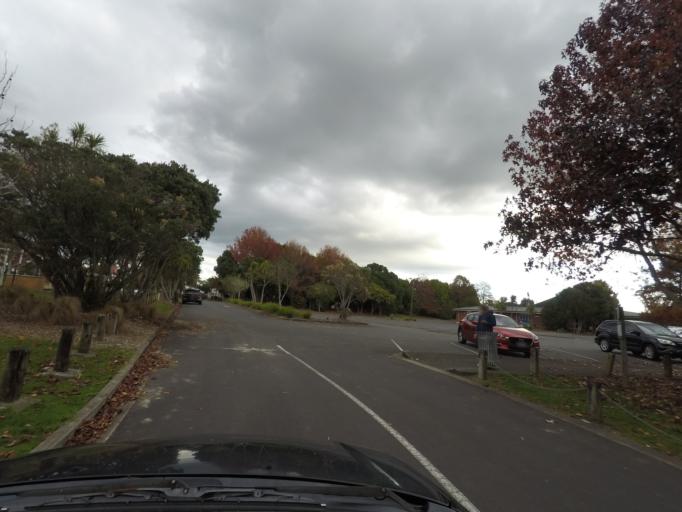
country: NZ
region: Auckland
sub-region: Auckland
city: Rosebank
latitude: -36.8284
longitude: 174.6301
